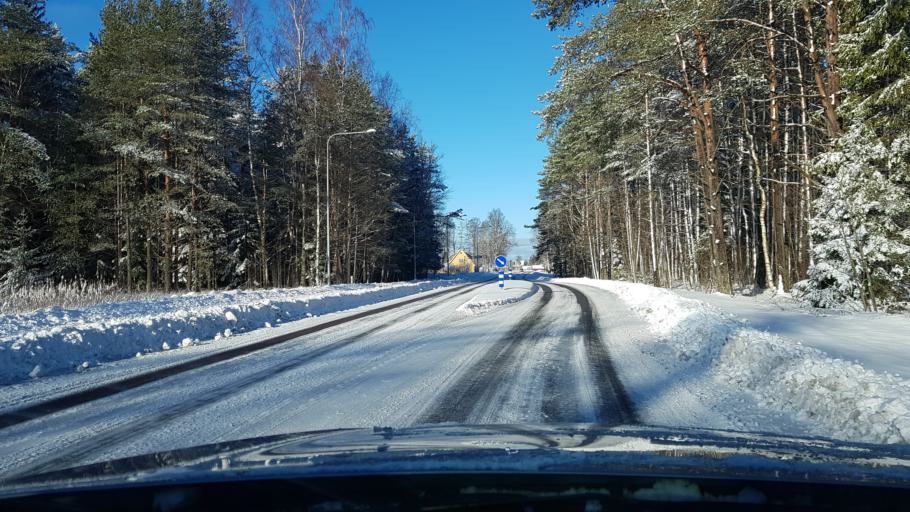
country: EE
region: Hiiumaa
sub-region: Kaerdla linn
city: Kardla
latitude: 58.9816
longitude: 22.7585
